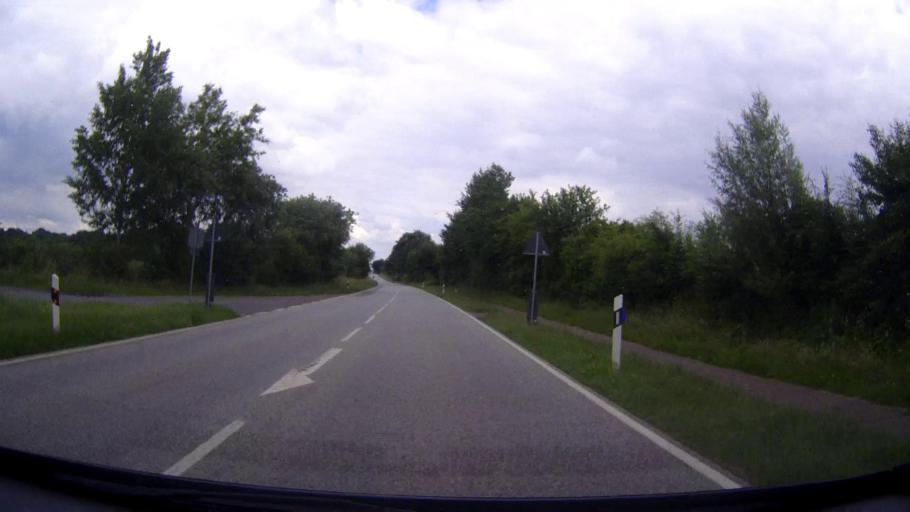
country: DE
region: Schleswig-Holstein
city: Hanerau-Hademarschen
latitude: 54.1241
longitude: 9.3905
